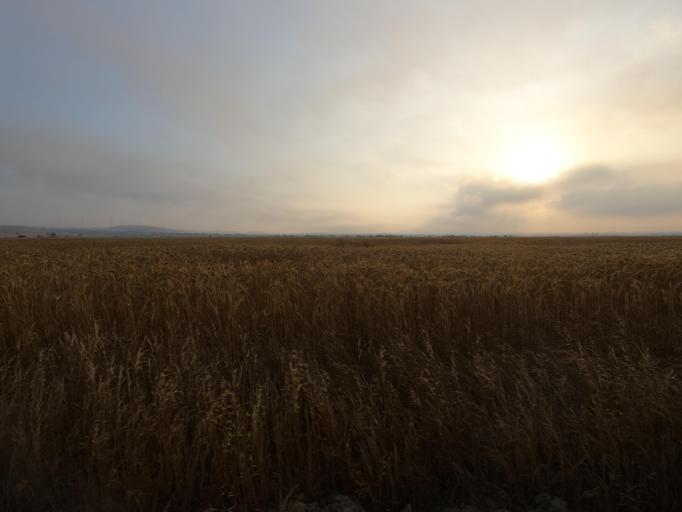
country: CY
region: Larnaka
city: Tersefanou
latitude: 34.8283
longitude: 33.5175
